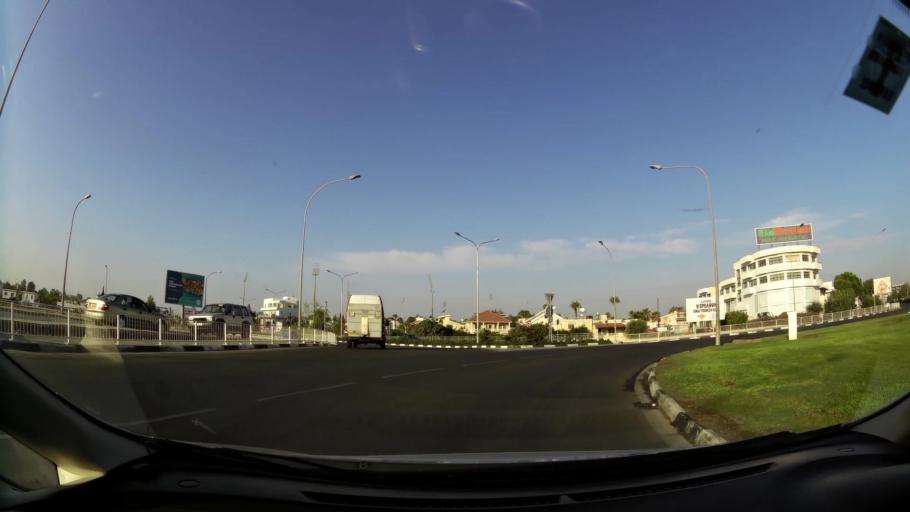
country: CY
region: Larnaka
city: Larnaca
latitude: 34.9281
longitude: 33.6041
